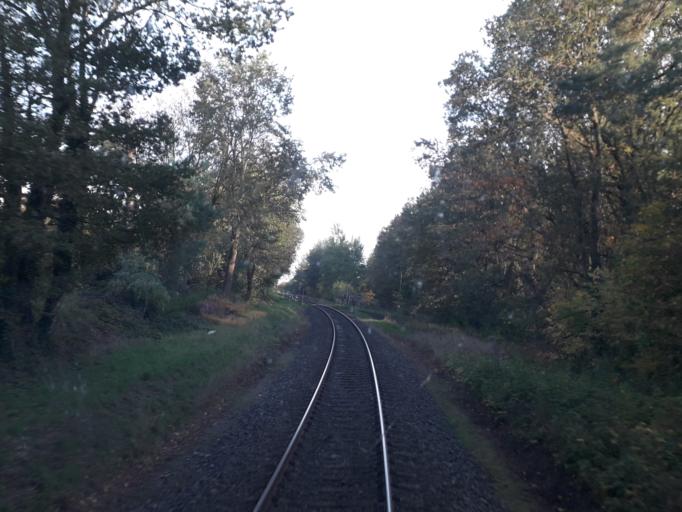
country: DE
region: Brandenburg
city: Perleberg
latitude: 53.0673
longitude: 11.8640
